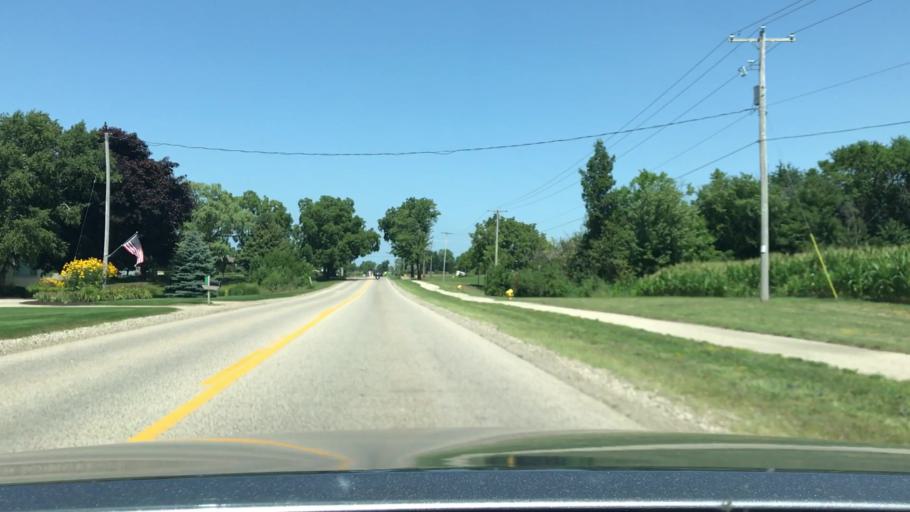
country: US
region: Michigan
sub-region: Ottawa County
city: Holland
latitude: 42.8462
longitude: -86.0790
